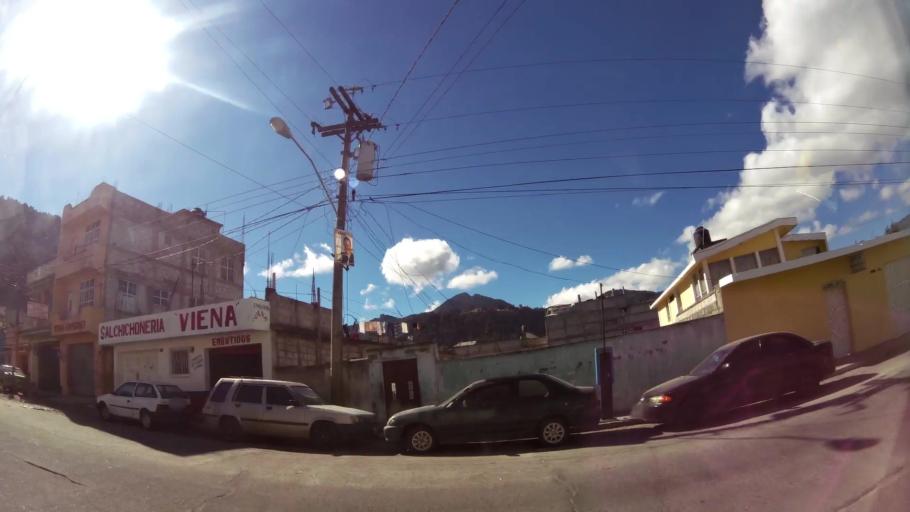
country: GT
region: Quetzaltenango
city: Quetzaltenango
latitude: 14.8352
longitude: -91.5085
